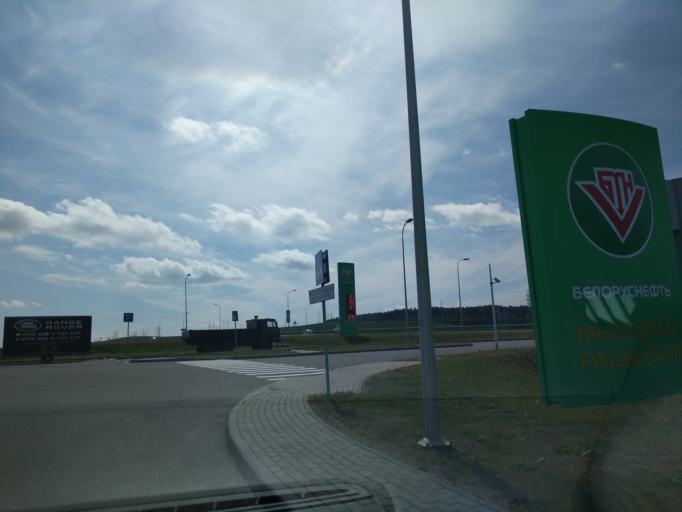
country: BY
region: Minsk
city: Bal'shavik
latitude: 54.0138
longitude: 27.5461
